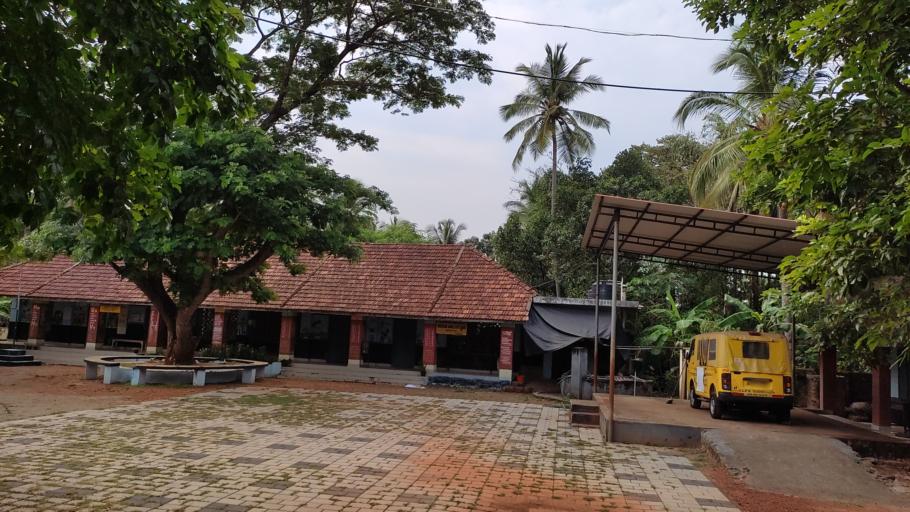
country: IN
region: Kerala
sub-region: Malappuram
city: Ponnani
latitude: 10.8396
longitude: 75.9889
